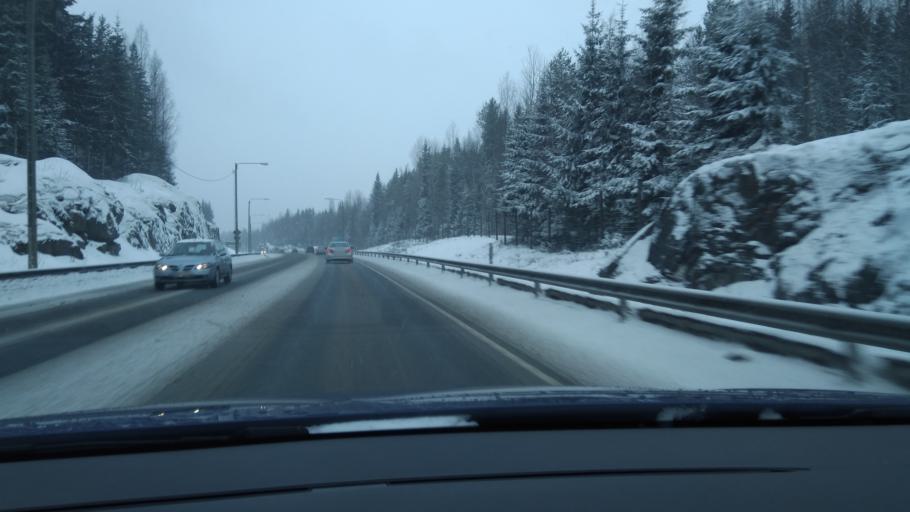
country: FI
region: Pirkanmaa
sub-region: Tampere
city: Kangasala
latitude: 61.5358
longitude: 23.9598
